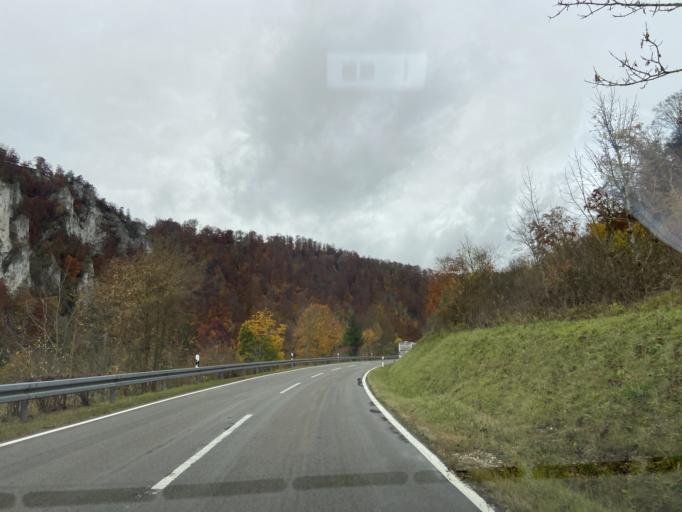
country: DE
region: Baden-Wuerttemberg
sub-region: Tuebingen Region
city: Stetten am Kalten Markt
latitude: 48.0852
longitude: 9.0711
